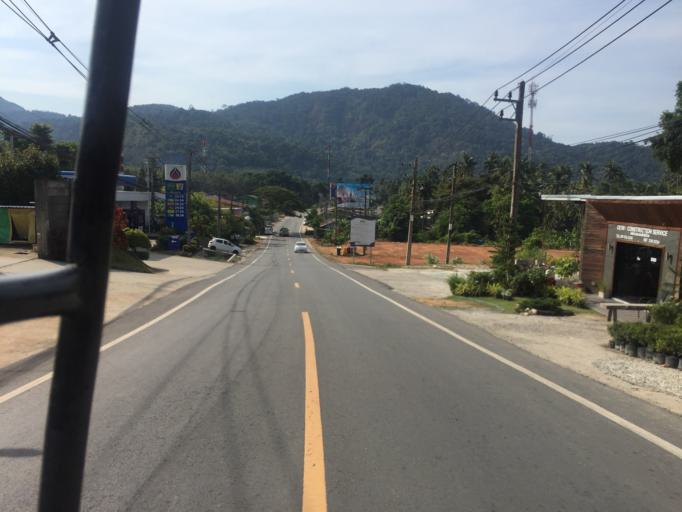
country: TH
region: Trat
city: Laem Ngop
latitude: 12.1359
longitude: 102.2761
